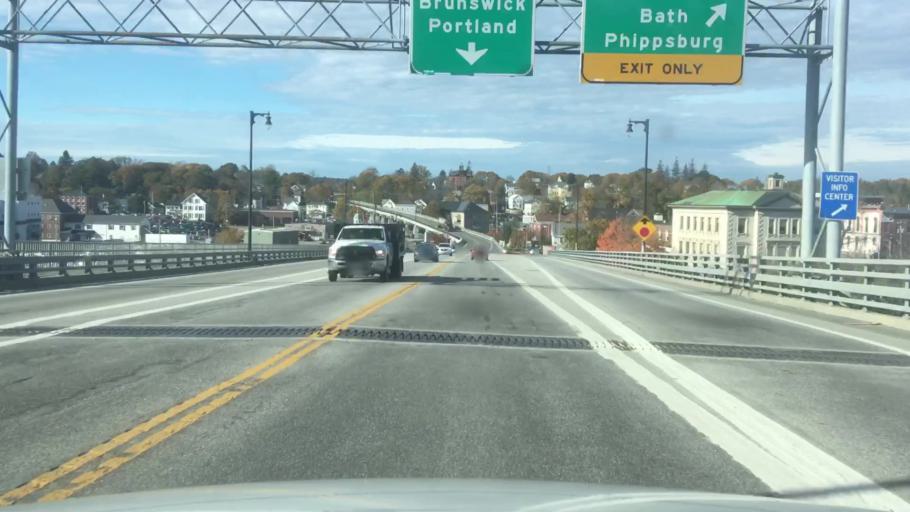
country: US
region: Maine
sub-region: Sagadahoc County
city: Bath
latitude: 43.9118
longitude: -69.8114
